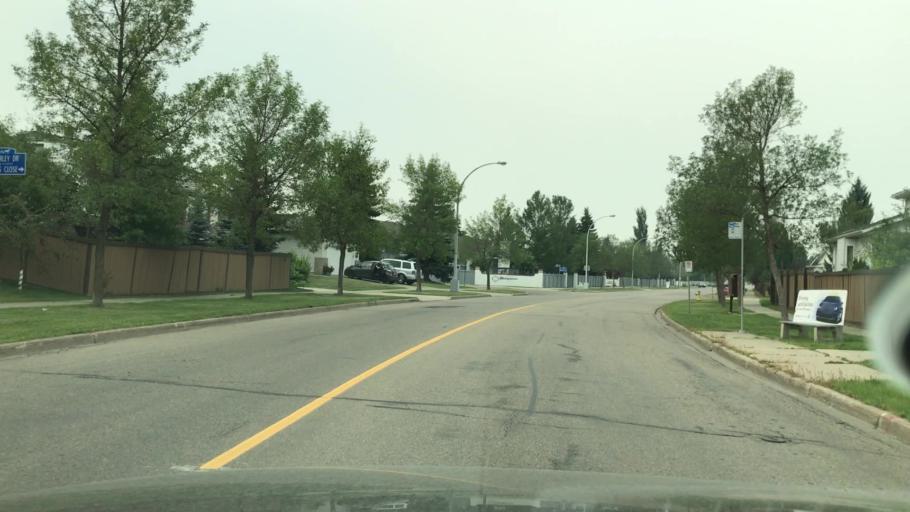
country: CA
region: Alberta
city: Edmonton
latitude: 53.4692
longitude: -113.5722
